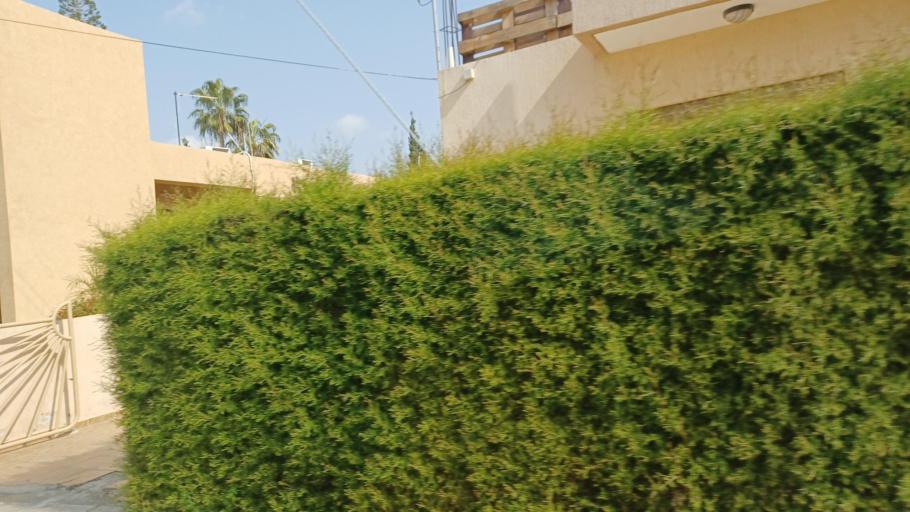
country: CY
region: Limassol
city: Ypsonas
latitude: 34.6853
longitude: 32.9694
